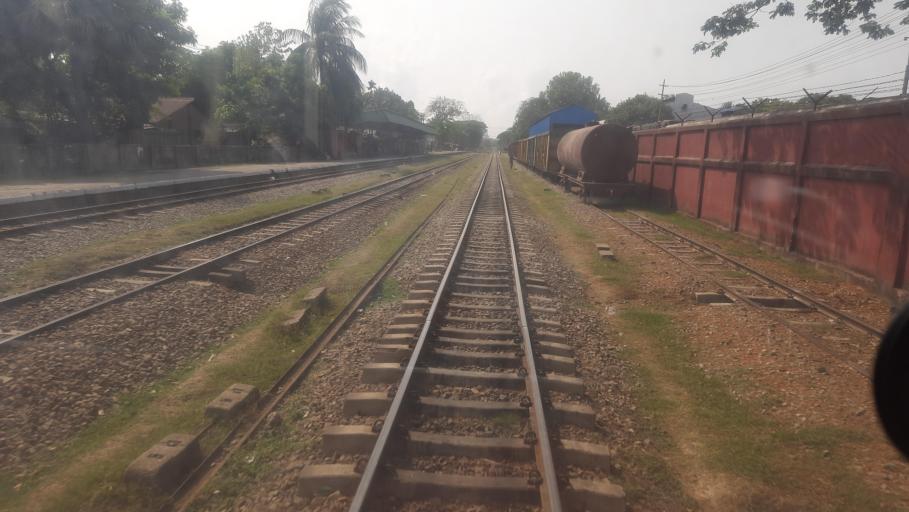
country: BD
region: Chittagong
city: Chittagong
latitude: 22.3538
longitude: 91.7963
